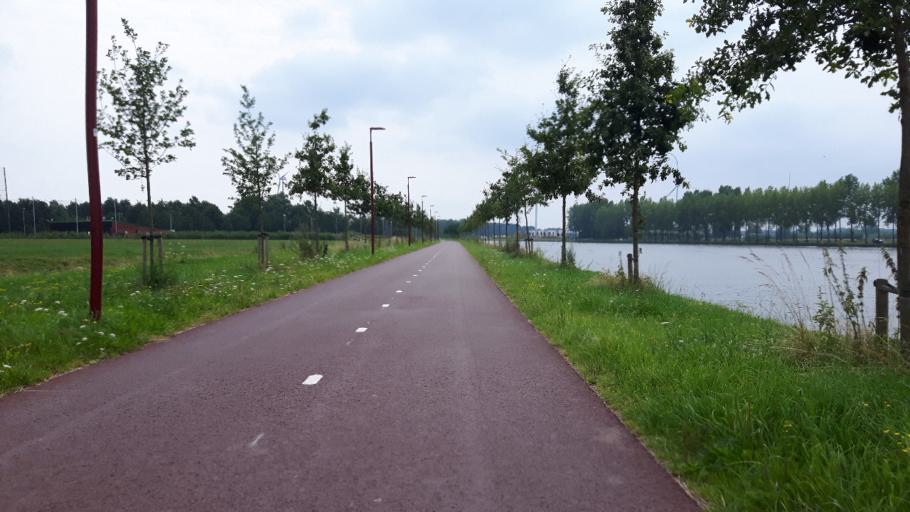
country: NL
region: Utrecht
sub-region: Gemeente Utrecht
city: Lunetten
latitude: 52.0340
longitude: 5.1196
